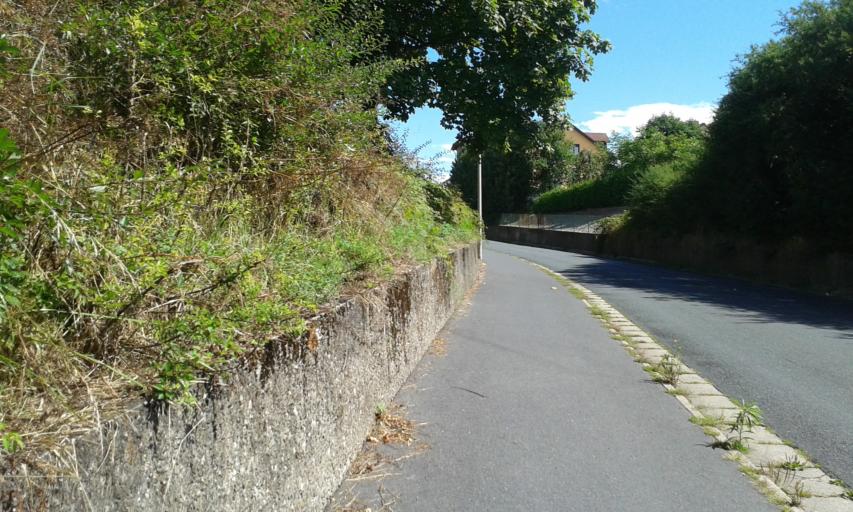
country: DE
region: Bavaria
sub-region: Upper Franconia
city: Kronach
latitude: 50.2381
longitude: 11.3351
